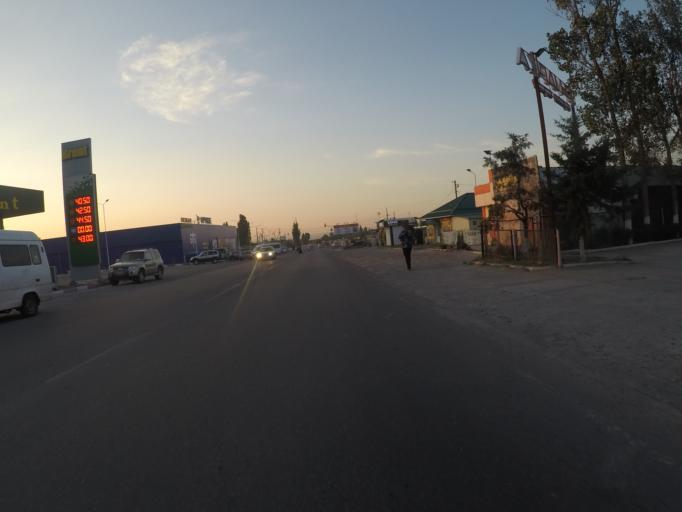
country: KG
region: Chuy
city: Lebedinovka
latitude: 42.8020
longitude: 74.6489
